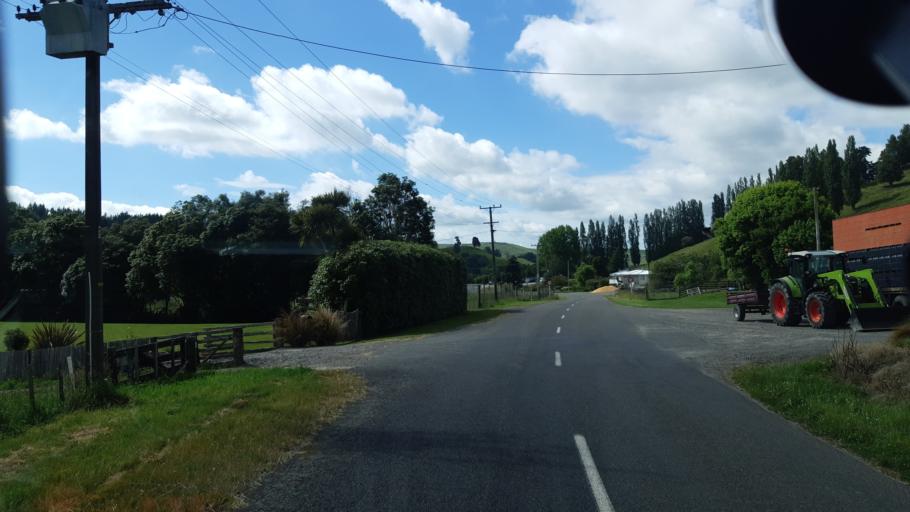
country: NZ
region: Manawatu-Wanganui
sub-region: Rangitikei District
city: Bulls
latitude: -39.9244
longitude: 175.5597
